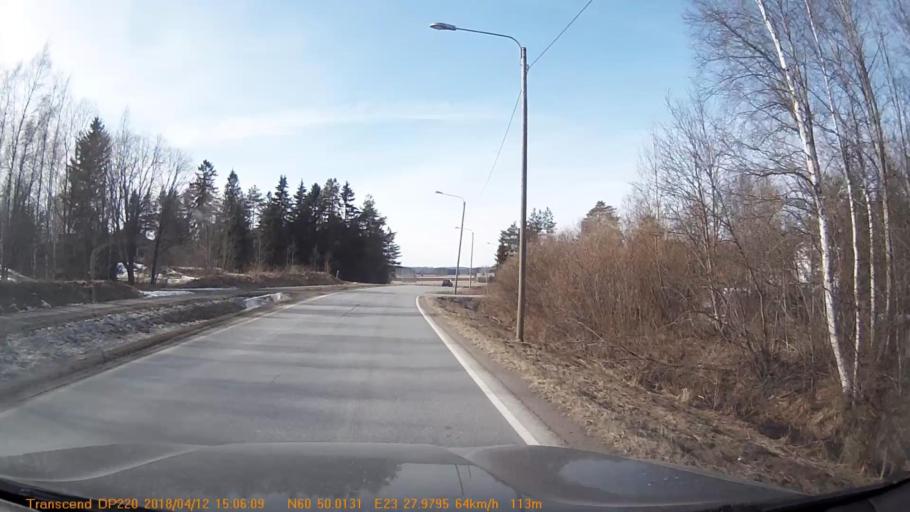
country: FI
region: Haeme
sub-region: Forssa
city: Jokioinen
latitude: 60.8338
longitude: 23.4658
